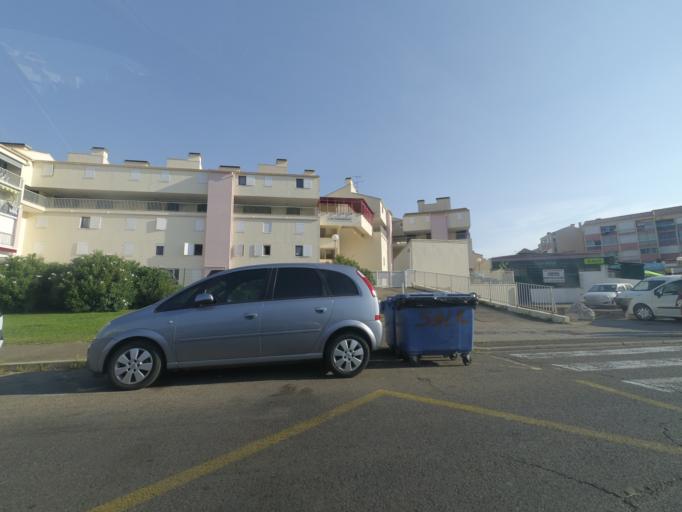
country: FR
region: Languedoc-Roussillon
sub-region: Departement du Gard
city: Le Grau-du-Roi
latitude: 43.5278
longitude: 4.1463
